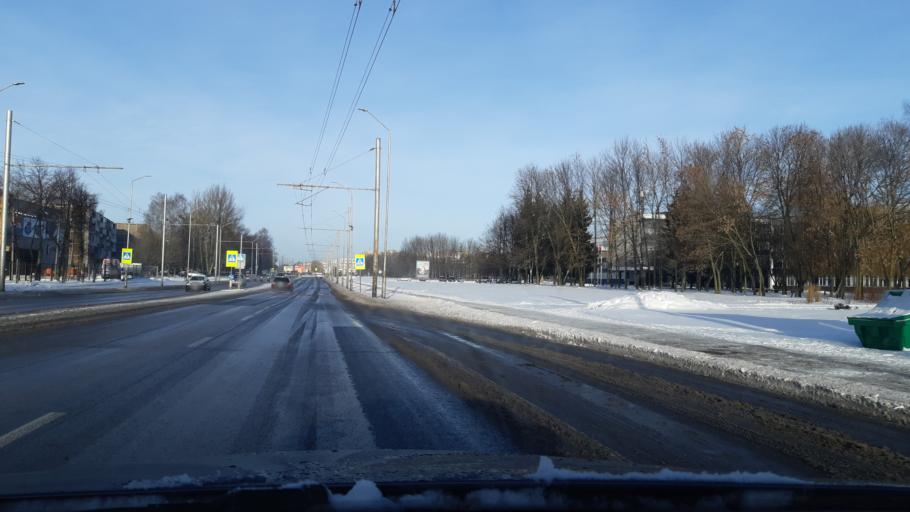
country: LT
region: Kauno apskritis
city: Dainava (Kaunas)
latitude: 54.9193
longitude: 23.9834
